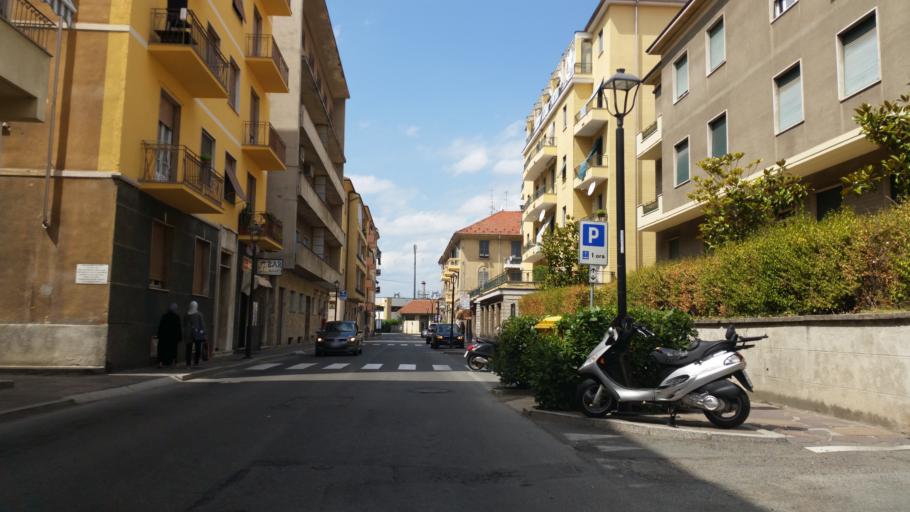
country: IT
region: Piedmont
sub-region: Provincia di Alessandria
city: Acqui Terme
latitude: 44.6711
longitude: 8.4649
